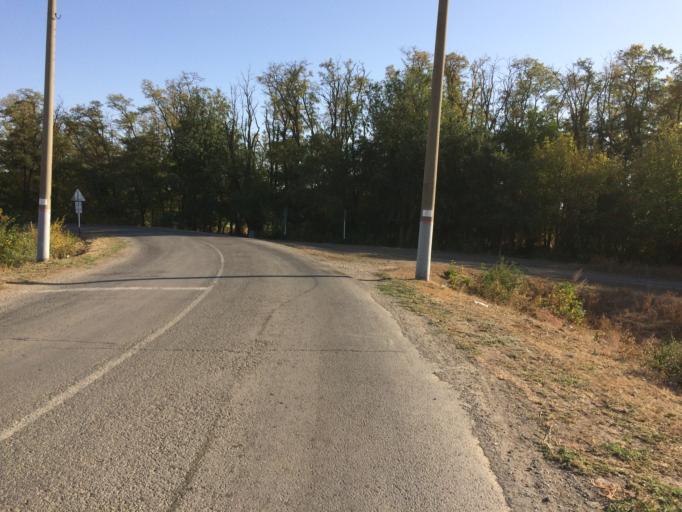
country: RU
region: Rostov
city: Tselina
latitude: 46.5283
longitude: 41.1879
